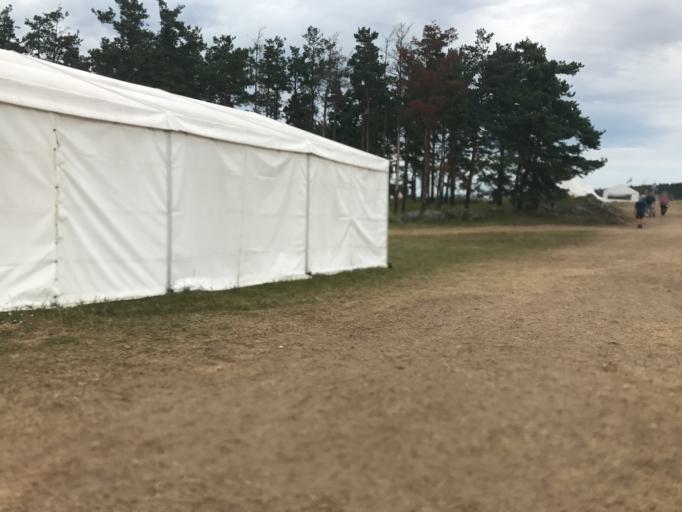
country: SE
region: Skane
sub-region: Kristianstads Kommun
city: Fjalkinge
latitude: 56.0066
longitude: 14.3020
